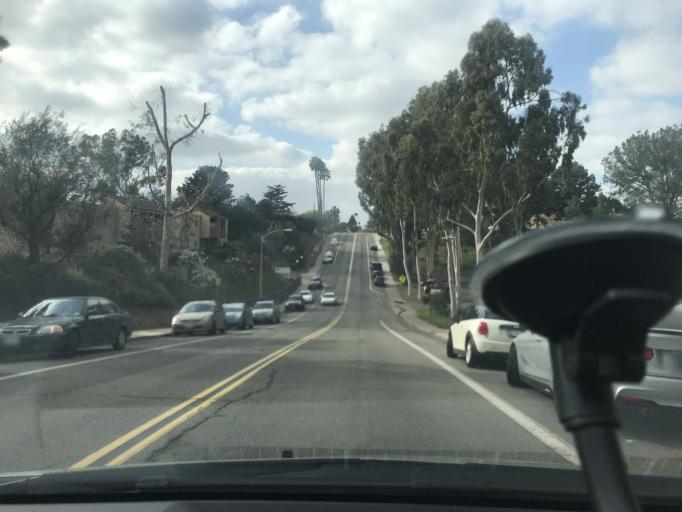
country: US
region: California
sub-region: San Diego County
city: San Diego
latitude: 32.8050
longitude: -117.1315
